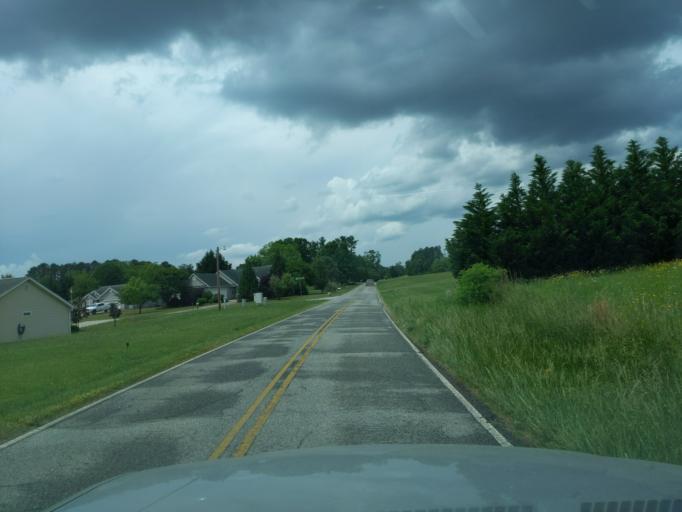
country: US
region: South Carolina
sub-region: Spartanburg County
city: Inman Mills
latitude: 35.0146
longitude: -82.1229
